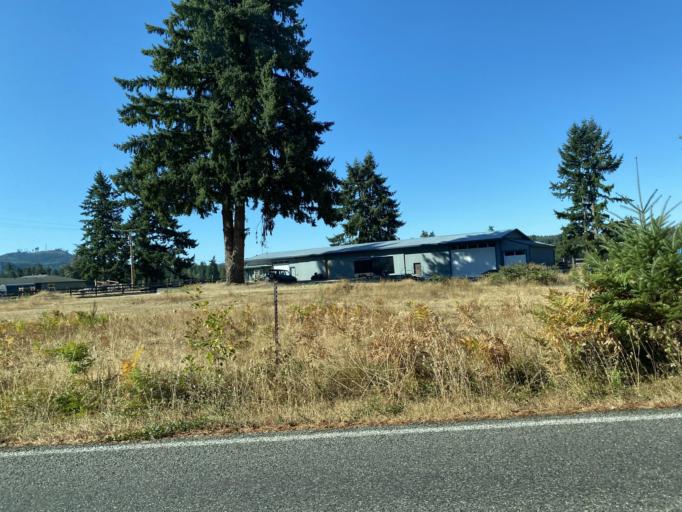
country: US
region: Washington
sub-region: Thurston County
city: Rainier
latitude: 46.8874
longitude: -122.7467
